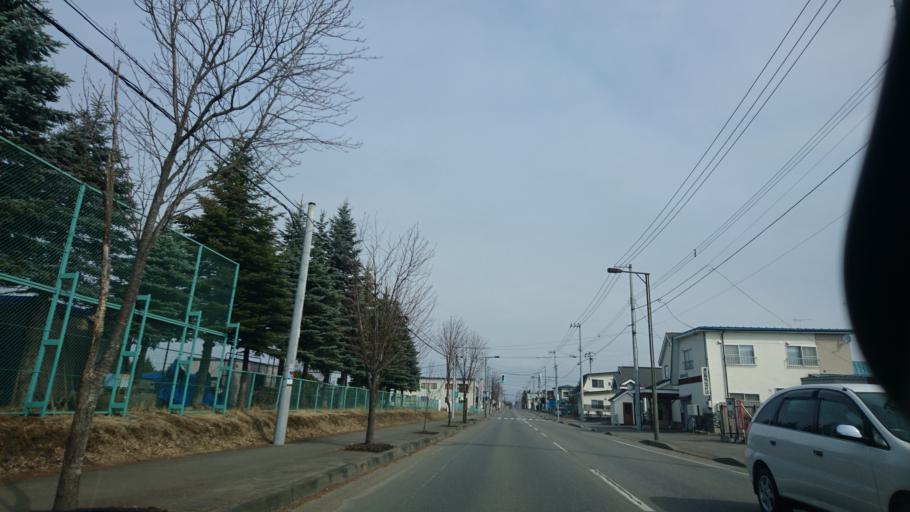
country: JP
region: Hokkaido
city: Otofuke
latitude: 42.9682
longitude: 143.2129
